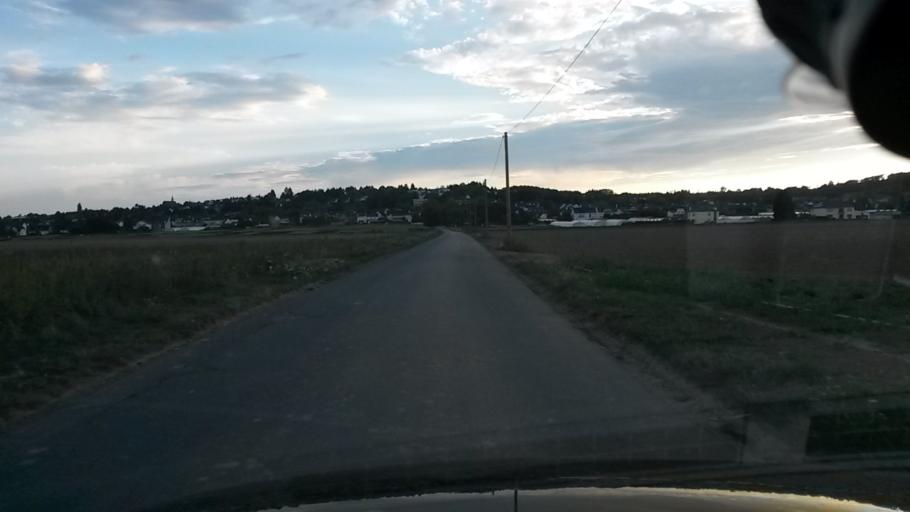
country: DE
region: North Rhine-Westphalia
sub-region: Regierungsbezirk Koln
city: Alfter
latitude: 50.7323
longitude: 7.0295
